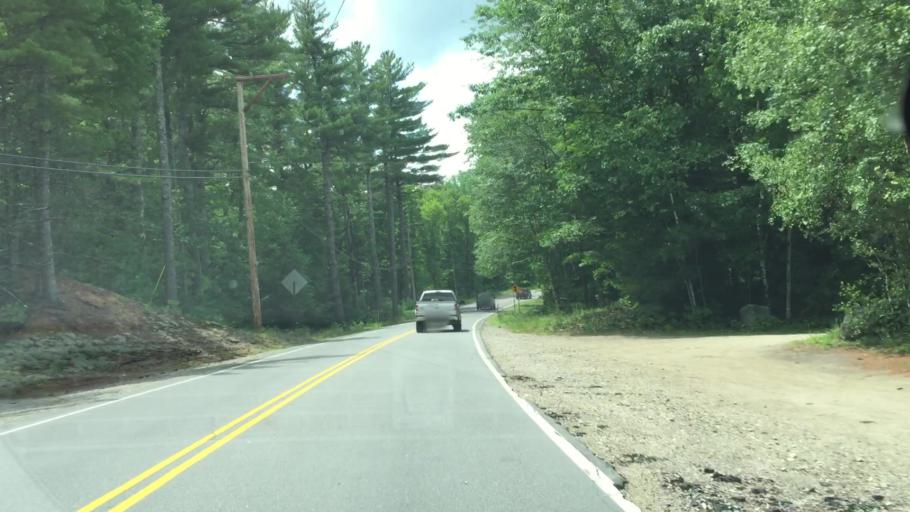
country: US
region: New Hampshire
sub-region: Grafton County
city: Holderness
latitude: 43.7422
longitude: -71.5788
